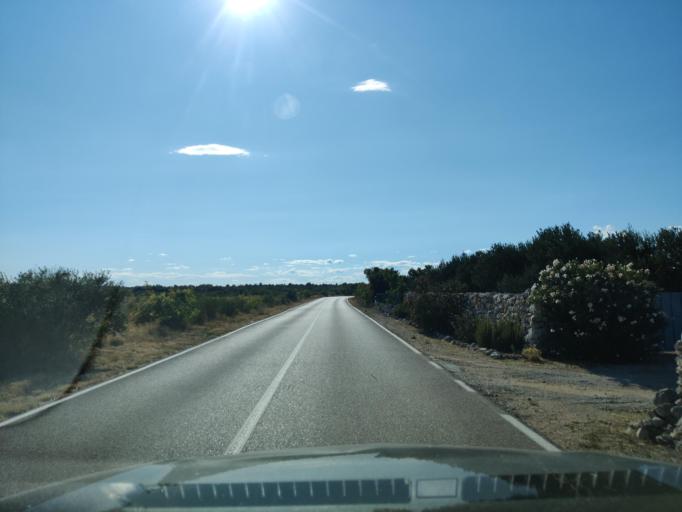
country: HR
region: Sibensko-Kniniska
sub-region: Grad Sibenik
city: Sibenik
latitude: 43.7413
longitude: 15.8569
